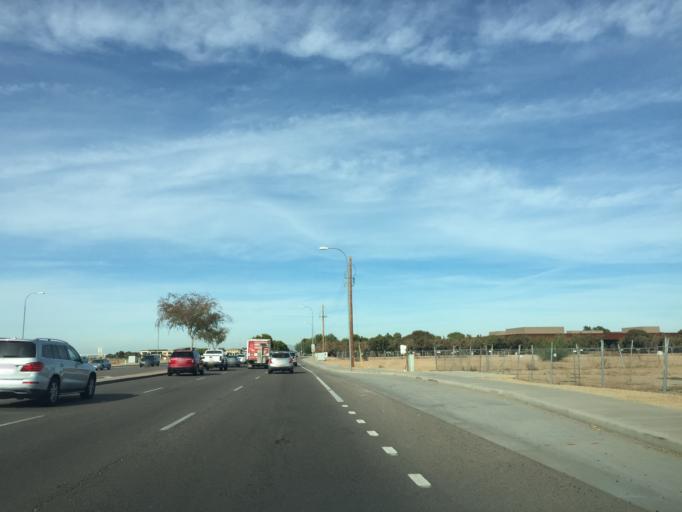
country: US
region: Arizona
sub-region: Maricopa County
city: Chandler
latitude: 33.2632
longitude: -111.7895
